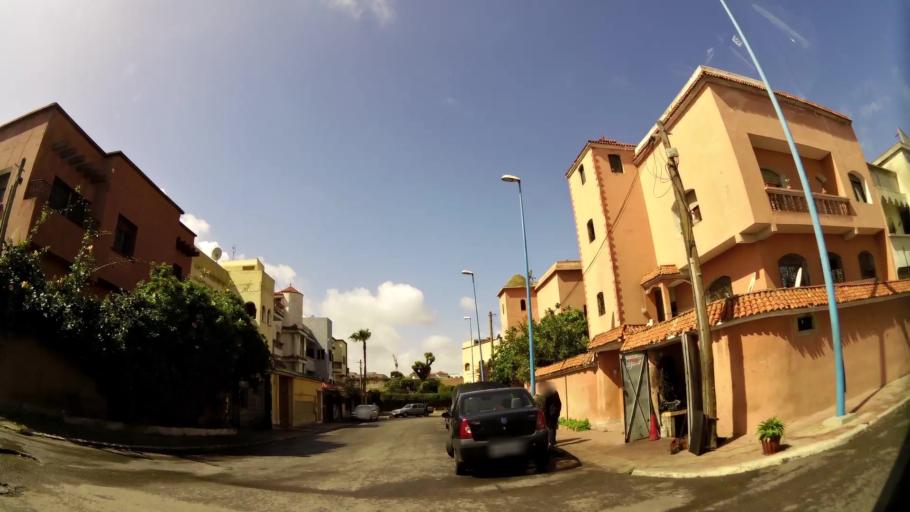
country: MA
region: Grand Casablanca
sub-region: Mediouna
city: Tit Mellil
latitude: 33.6162
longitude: -7.5223
